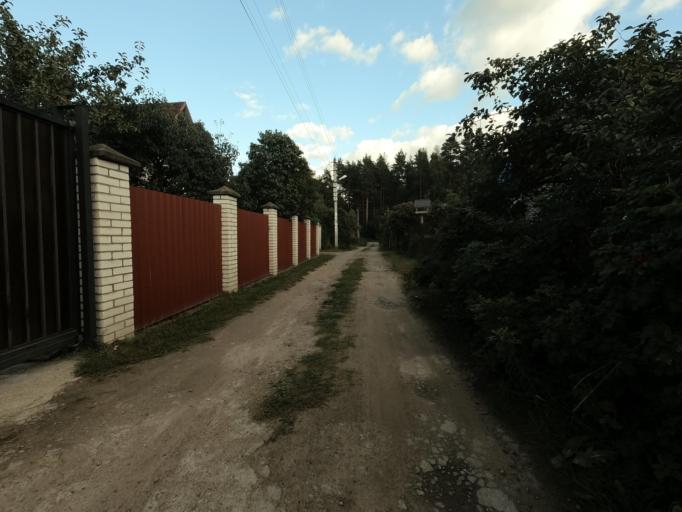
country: RU
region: Leningrad
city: Imeni Sverdlova
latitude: 59.8387
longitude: 30.7085
